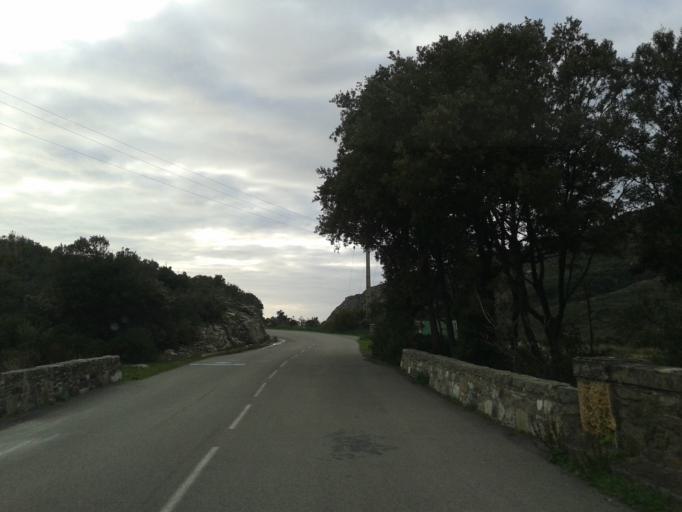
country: FR
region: Corsica
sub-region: Departement de la Haute-Corse
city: Brando
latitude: 42.8649
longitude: 9.3477
